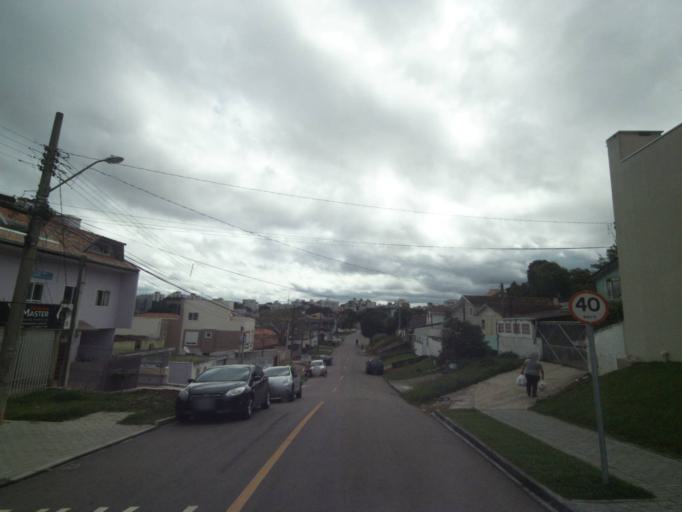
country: BR
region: Parana
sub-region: Curitiba
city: Curitiba
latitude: -25.4779
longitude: -49.2807
